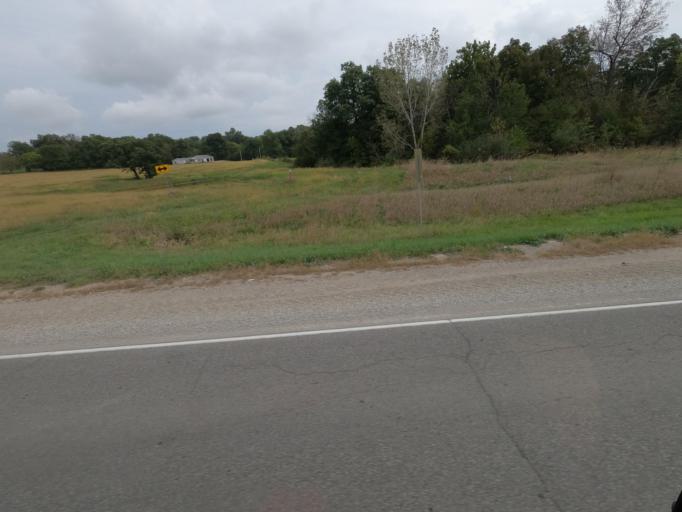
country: US
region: Iowa
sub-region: Wapello County
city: Ottumwa
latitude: 40.9253
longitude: -92.2301
